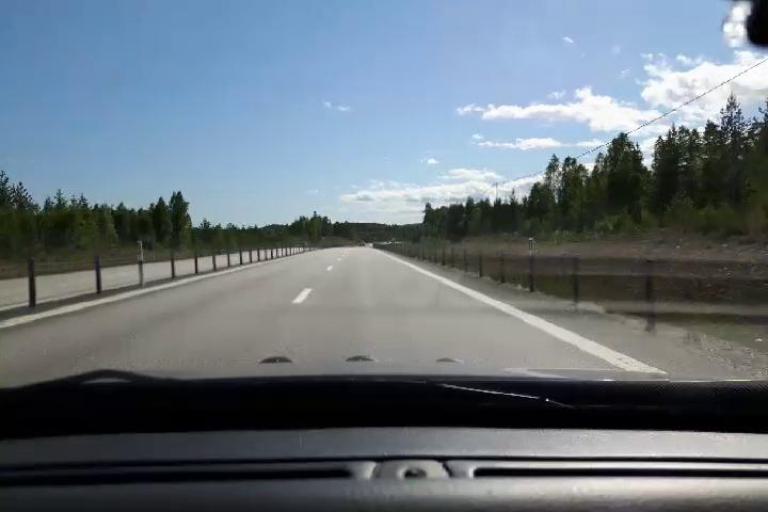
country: SE
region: Gaevleborg
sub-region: Hudiksvalls Kommun
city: Iggesund
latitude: 61.6736
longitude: 17.0325
